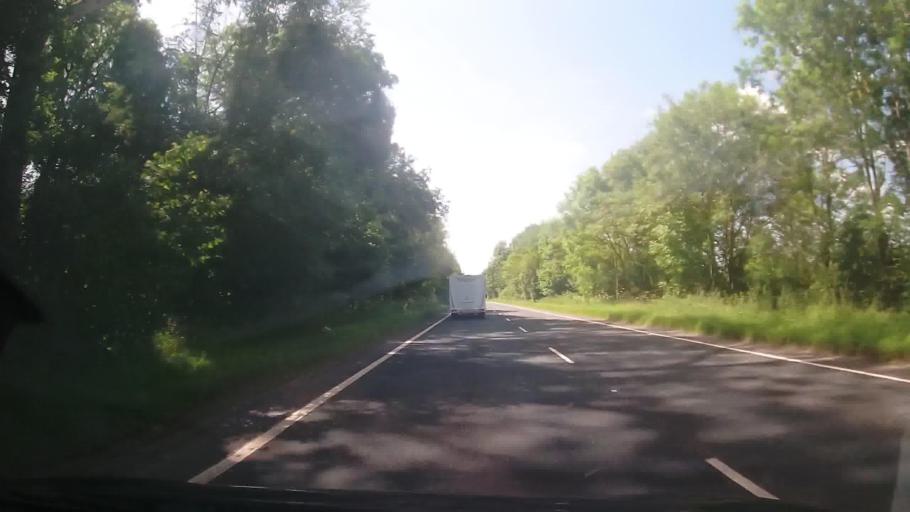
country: GB
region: England
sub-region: Shropshire
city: Ludlow
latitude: 52.3490
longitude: -2.7073
